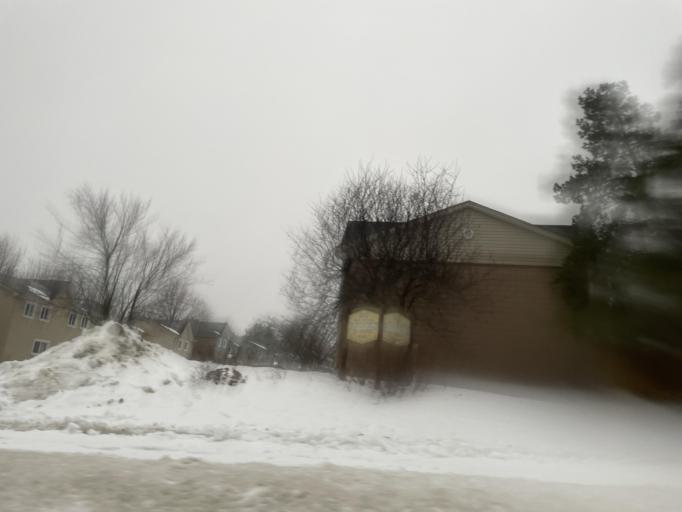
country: CA
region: Ontario
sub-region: Wellington County
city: Guelph
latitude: 43.5327
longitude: -80.2856
